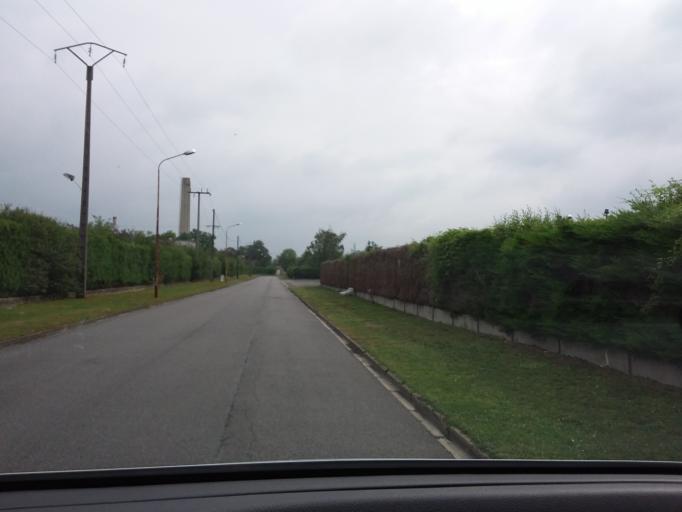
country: FR
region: Picardie
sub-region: Departement de l'Aisne
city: Laon
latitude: 49.5863
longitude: 3.6441
